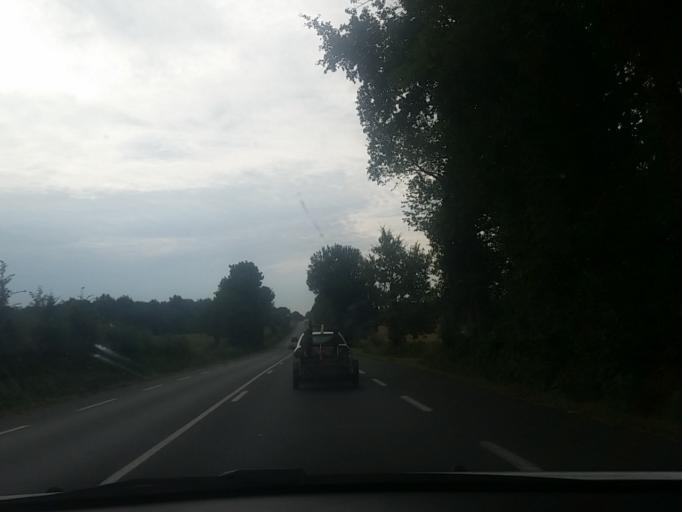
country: FR
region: Pays de la Loire
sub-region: Departement de la Vendee
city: Chavagnes-en-Paillers
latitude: 46.8850
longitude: -1.2145
